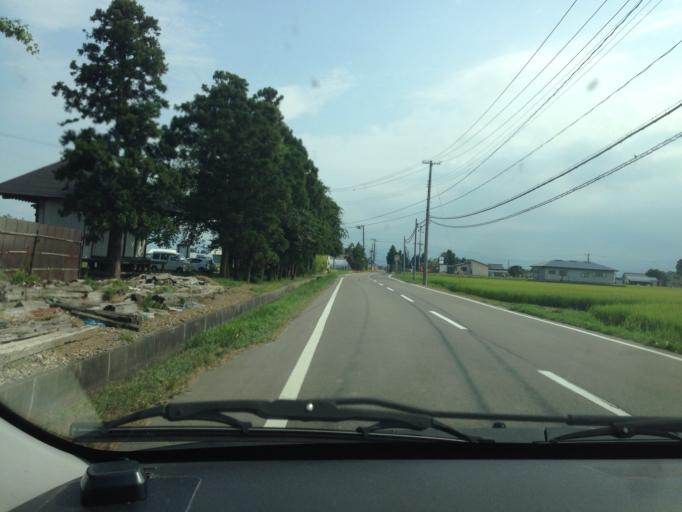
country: JP
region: Fukushima
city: Kitakata
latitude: 37.5707
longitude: 139.8534
